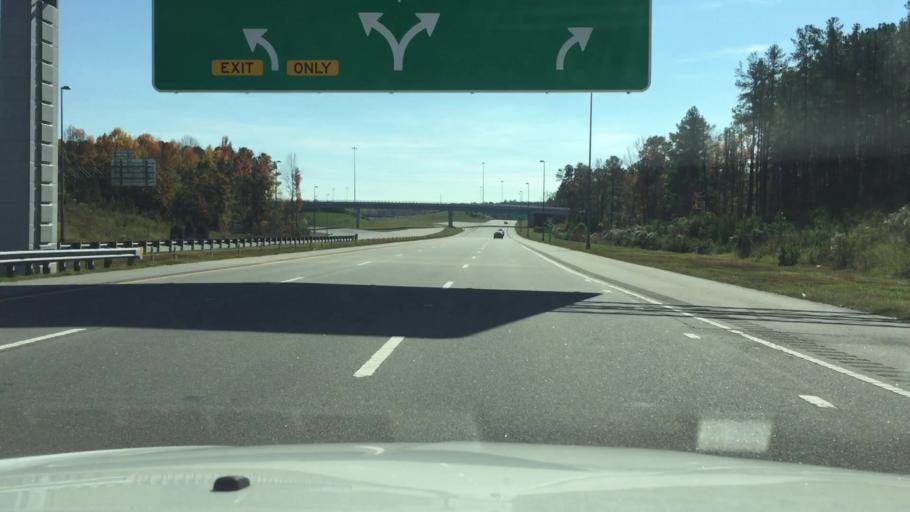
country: US
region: North Carolina
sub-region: Wake County
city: Morrisville
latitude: 35.8622
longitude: -78.8643
